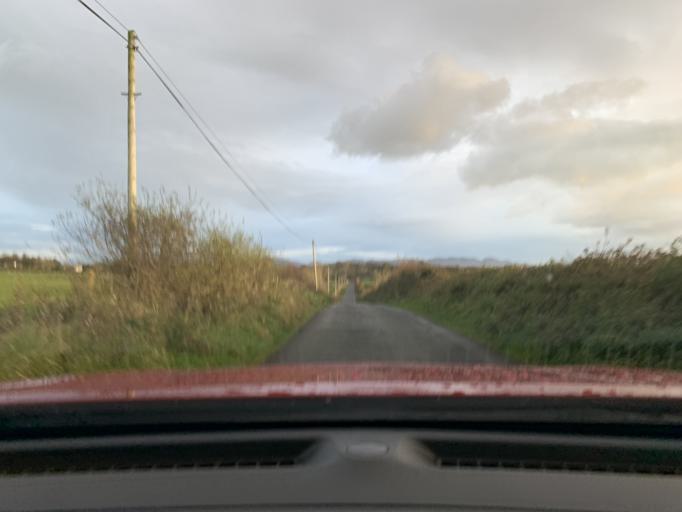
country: IE
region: Connaught
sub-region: Sligo
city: Sligo
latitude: 54.3070
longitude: -8.4989
